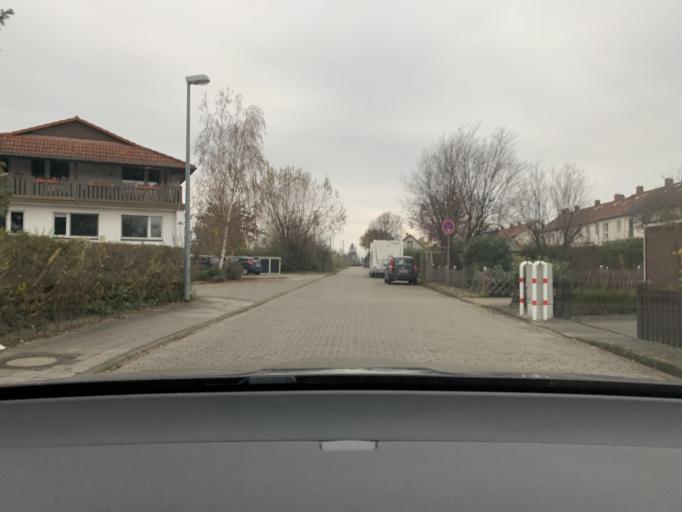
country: DE
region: Lower Saxony
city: Vordorf
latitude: 52.3174
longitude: 10.5099
